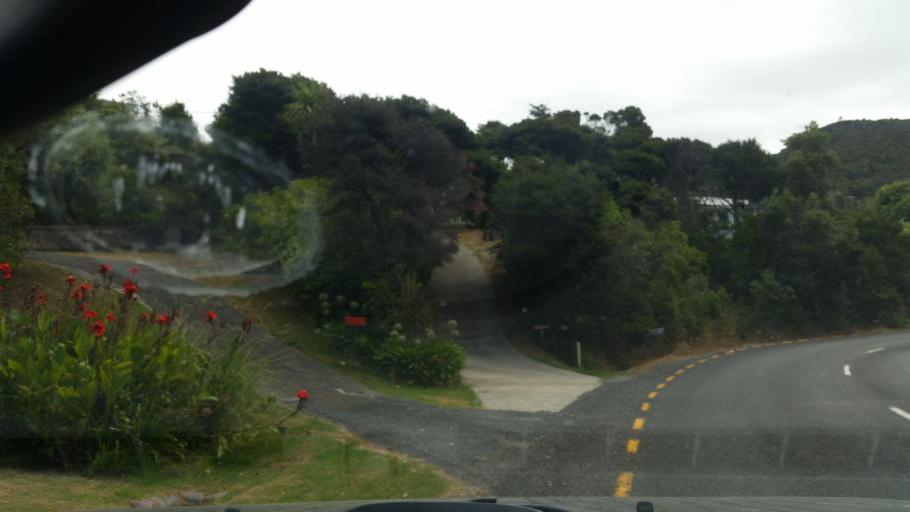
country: NZ
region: Auckland
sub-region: Auckland
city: Wellsford
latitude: -36.0826
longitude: 174.5891
